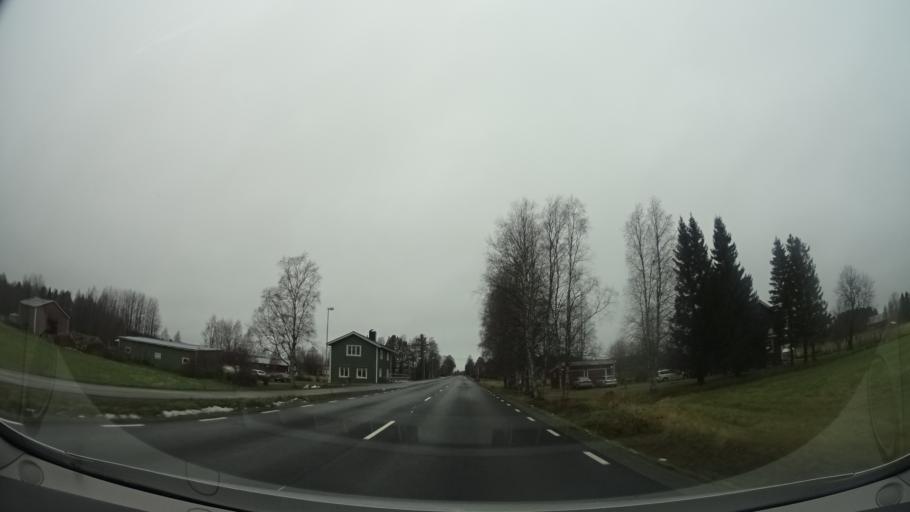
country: SE
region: Vaesterbotten
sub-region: Skelleftea Kommun
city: Kage
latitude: 64.8379
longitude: 20.9632
